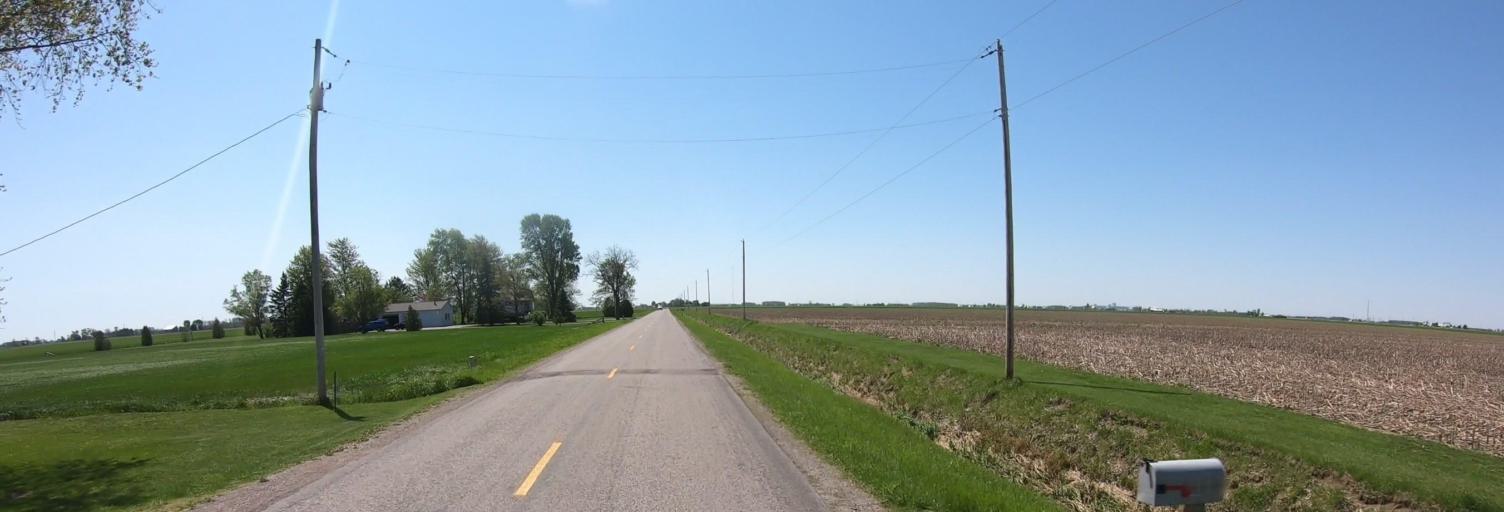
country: US
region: Ohio
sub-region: Henry County
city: Deshler
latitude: 41.1939
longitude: -83.9006
